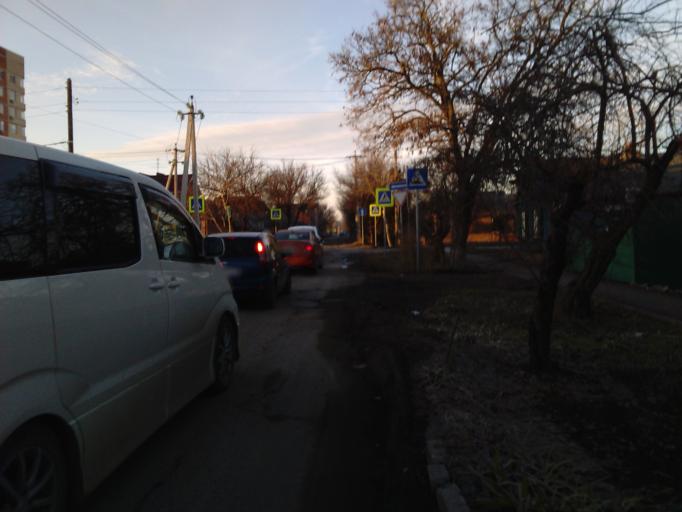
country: RU
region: Rostov
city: Bataysk
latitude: 47.1428
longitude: 39.7440
